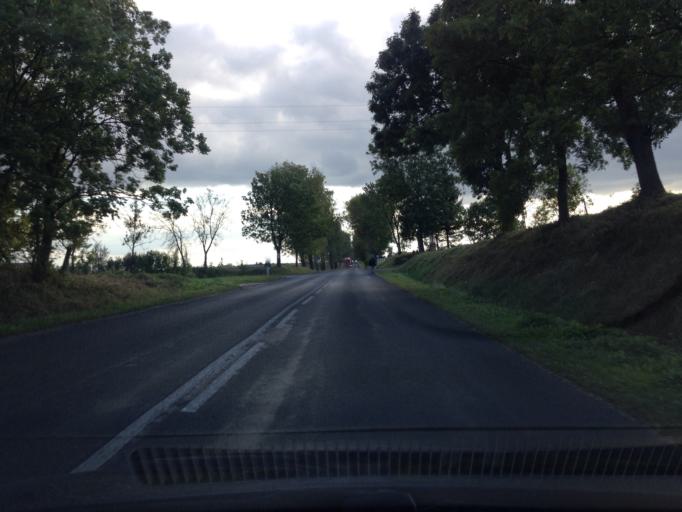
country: PL
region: Kujawsko-Pomorskie
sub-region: Powiat rypinski
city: Rypin
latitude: 53.0383
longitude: 19.3662
